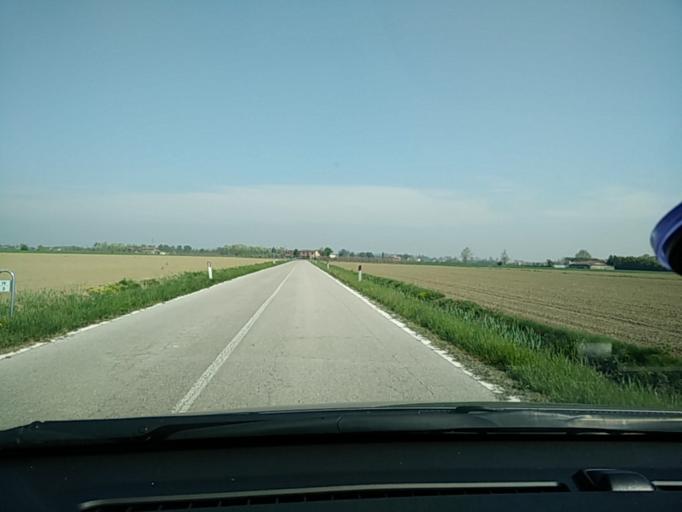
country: IT
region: Veneto
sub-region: Provincia di Treviso
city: Zenson di Piave
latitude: 45.6718
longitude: 12.4627
